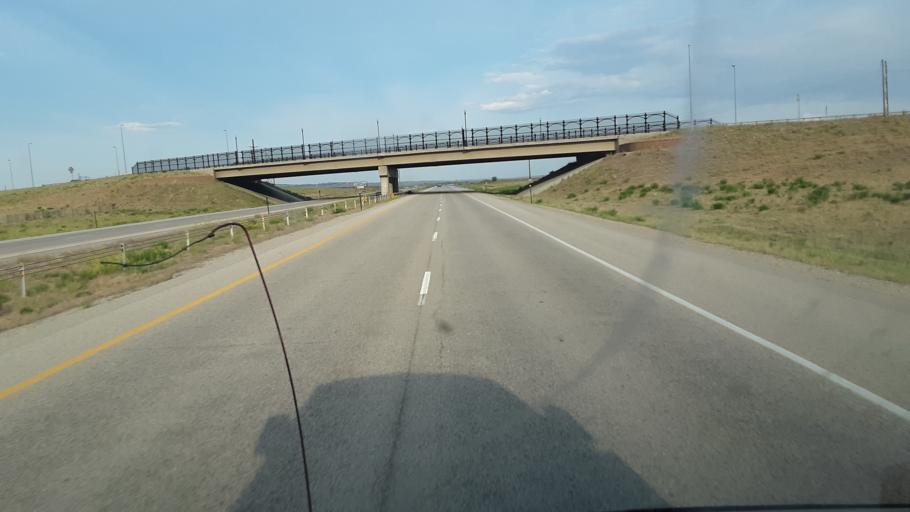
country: US
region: Wyoming
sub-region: Natrona County
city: Mills
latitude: 42.8652
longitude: -106.3587
